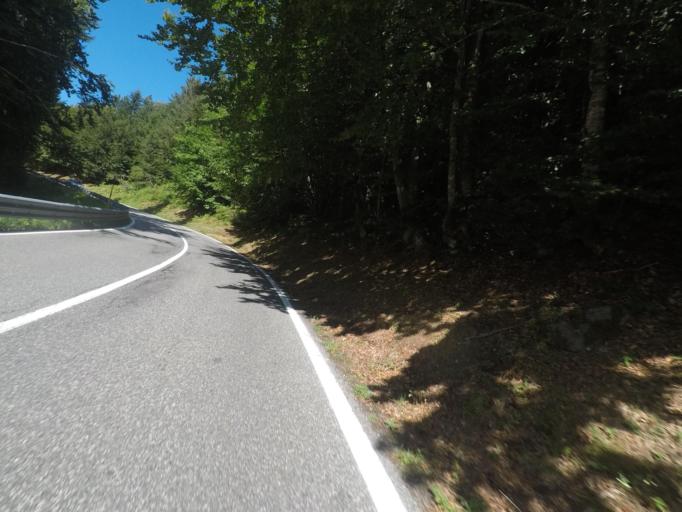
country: IT
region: Tuscany
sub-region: Provincia di Massa-Carrara
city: Comano
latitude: 44.2934
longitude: 10.2059
